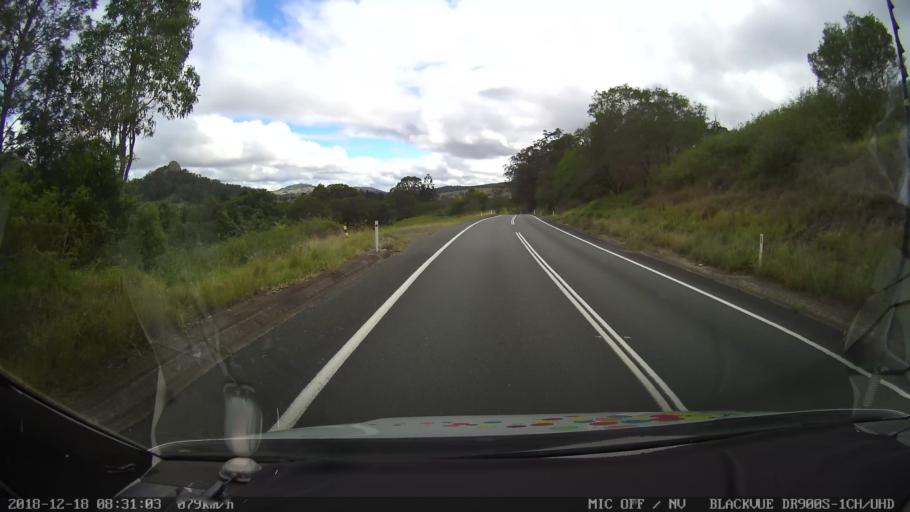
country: AU
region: New South Wales
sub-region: Kyogle
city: Kyogle
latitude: -28.3169
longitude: 152.7746
